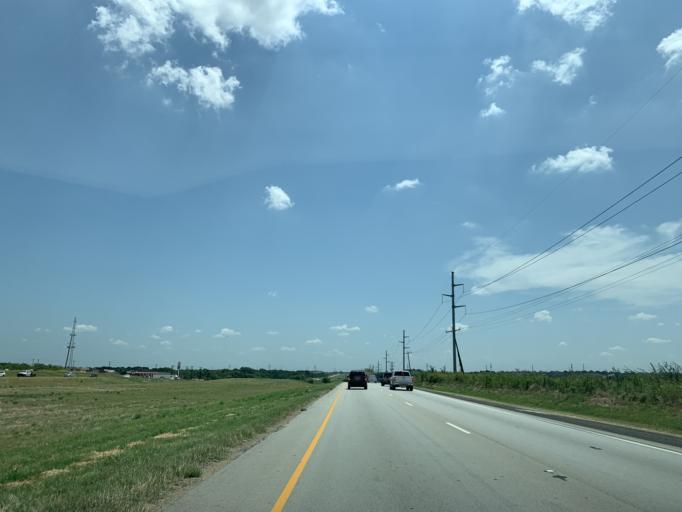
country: US
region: Texas
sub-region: Denton County
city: Roanoke
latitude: 33.0249
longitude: -97.2623
